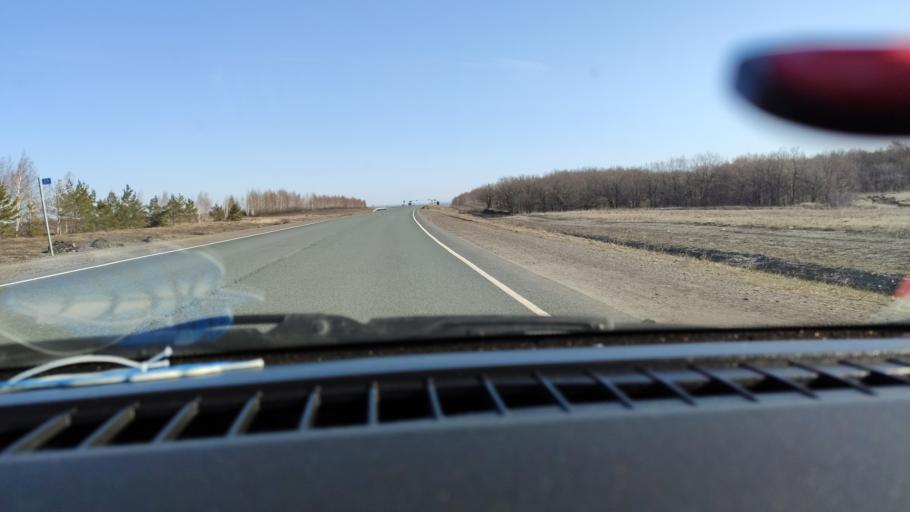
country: RU
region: Samara
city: Syzran'
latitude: 52.9472
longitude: 48.3044
